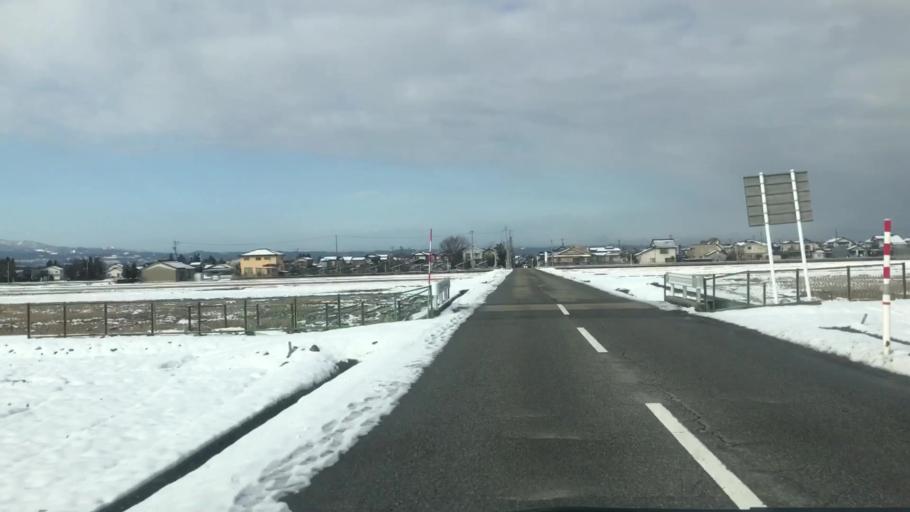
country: JP
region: Toyama
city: Toyama-shi
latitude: 36.6141
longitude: 137.2616
